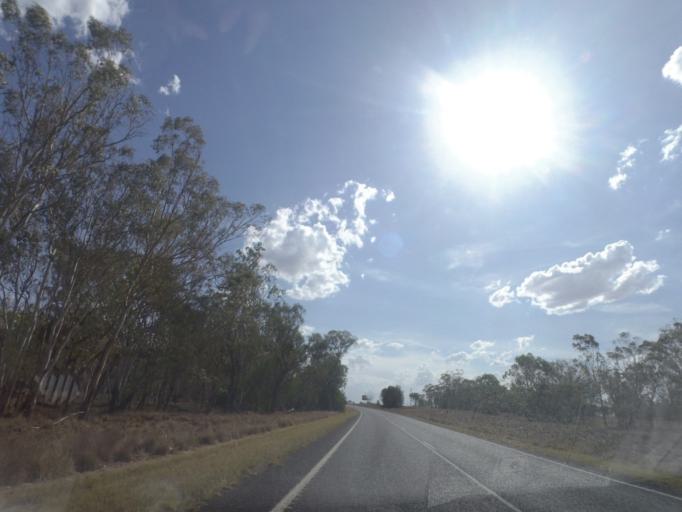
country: AU
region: New South Wales
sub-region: Moree Plains
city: Boggabilla
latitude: -28.5480
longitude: 150.8722
